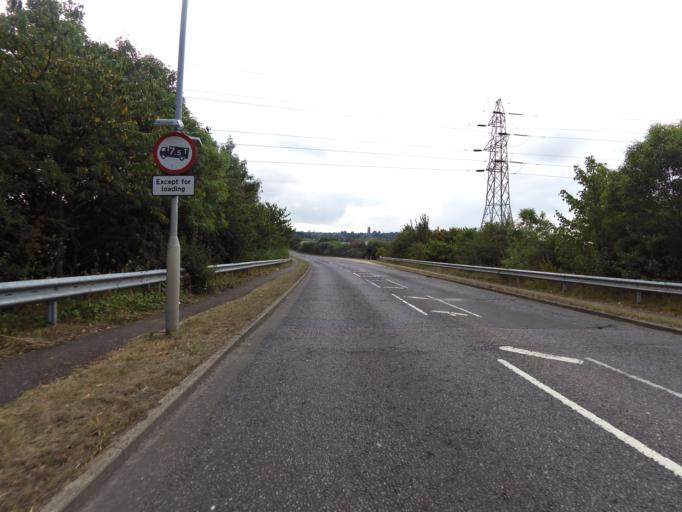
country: GB
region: England
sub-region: Hertfordshire
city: Shenley AV
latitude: 51.7092
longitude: -0.2945
